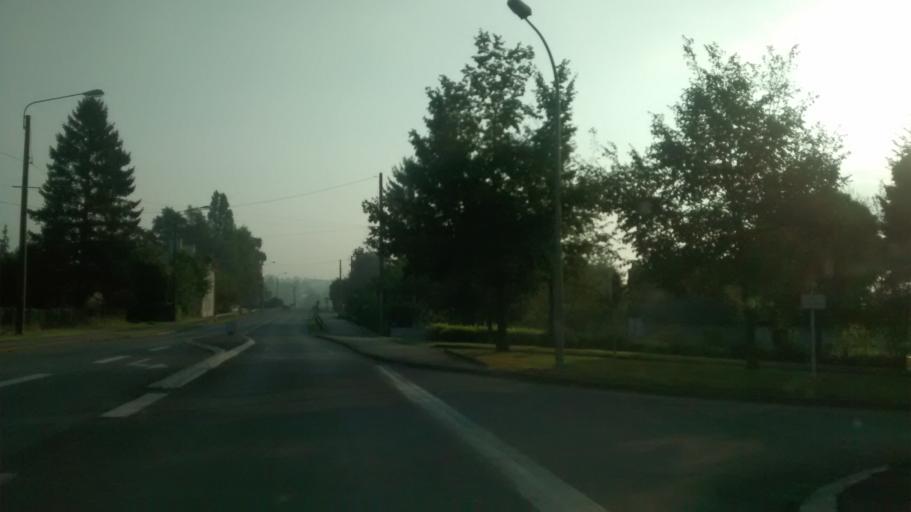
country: FR
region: Brittany
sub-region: Departement d'Ille-et-Vilaine
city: Saint-Didier
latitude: 48.1130
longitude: -1.3787
